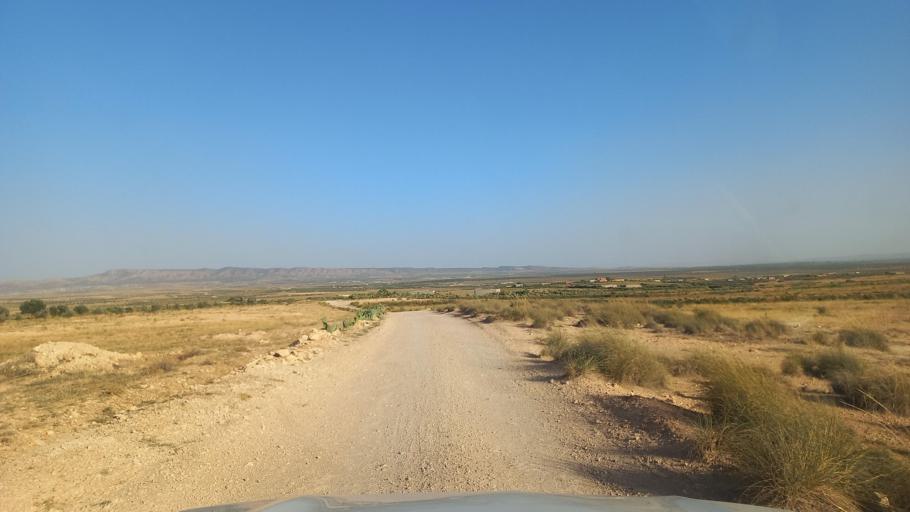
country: TN
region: Al Qasrayn
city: Sbiba
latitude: 35.3676
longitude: 9.0096
